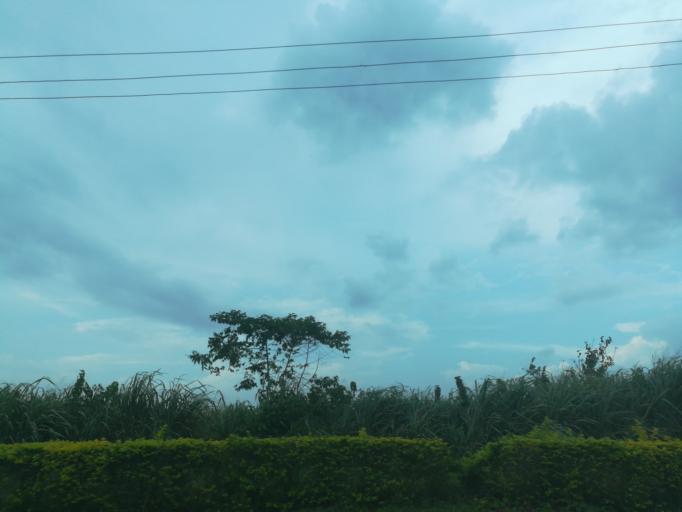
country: NG
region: Lagos
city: Ikorodu
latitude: 6.6358
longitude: 3.5285
